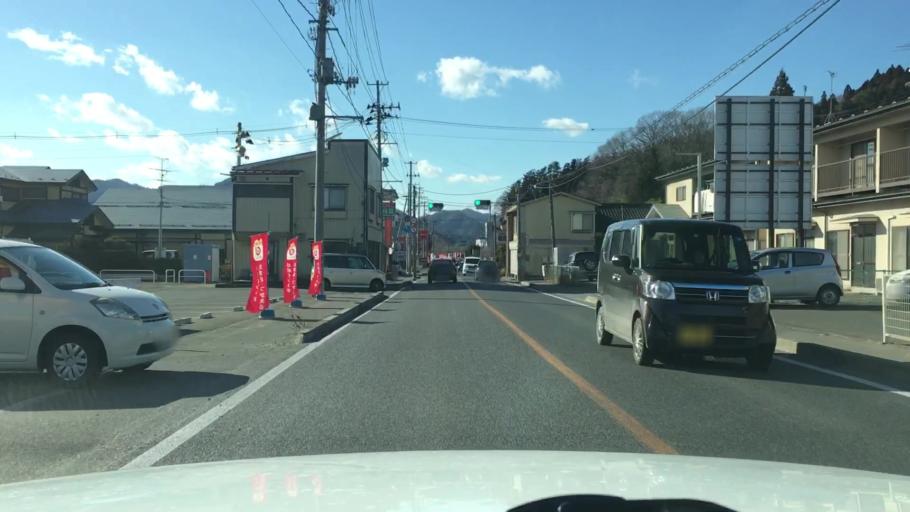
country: JP
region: Iwate
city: Miyako
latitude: 39.6320
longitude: 141.9132
